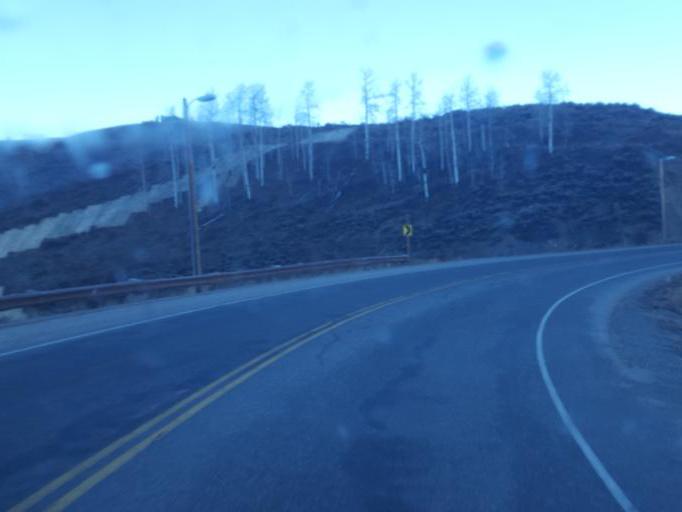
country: US
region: Colorado
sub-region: Gunnison County
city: Crested Butte
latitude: 38.8921
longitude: -106.9732
